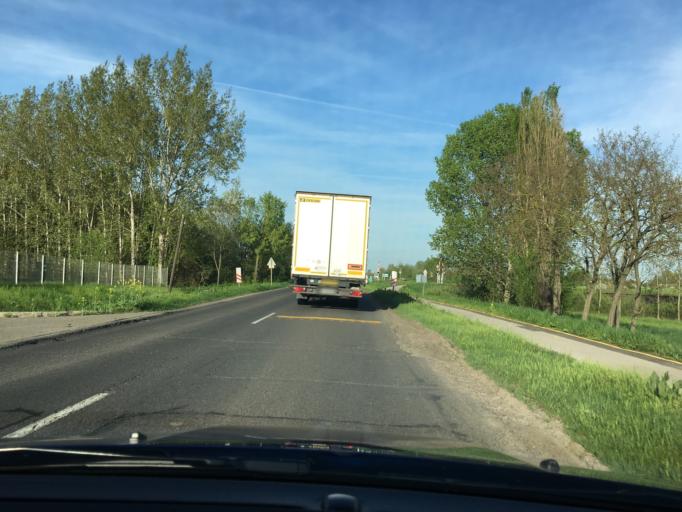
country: HU
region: Bekes
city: Szeghalom
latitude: 47.0106
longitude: 21.1354
